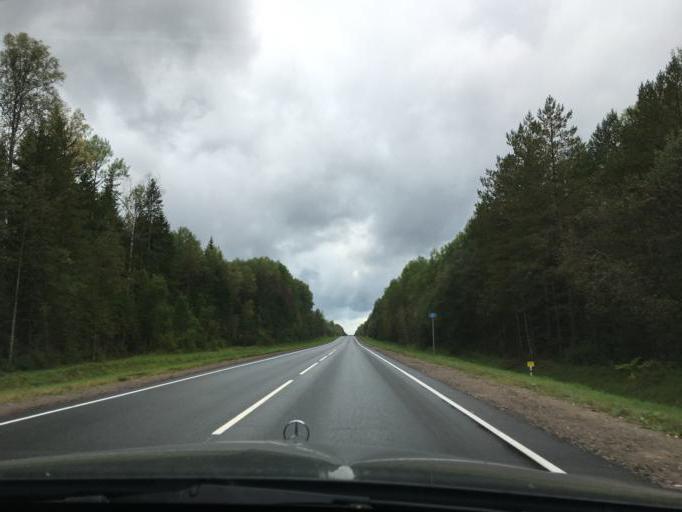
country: RU
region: Tverskaya
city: Nelidovo
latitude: 56.2667
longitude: 32.9258
